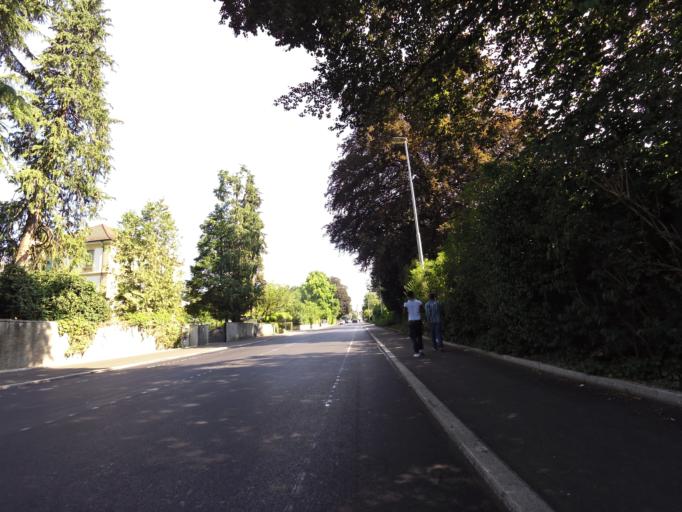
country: CH
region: Zug
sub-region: Zug
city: Zug
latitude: 47.1617
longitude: 8.5134
